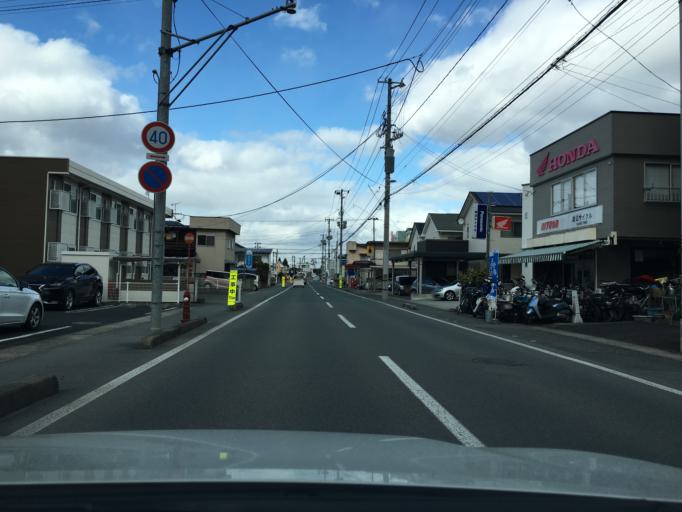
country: JP
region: Yamagata
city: Yamagata-shi
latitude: 38.2504
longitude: 140.3140
